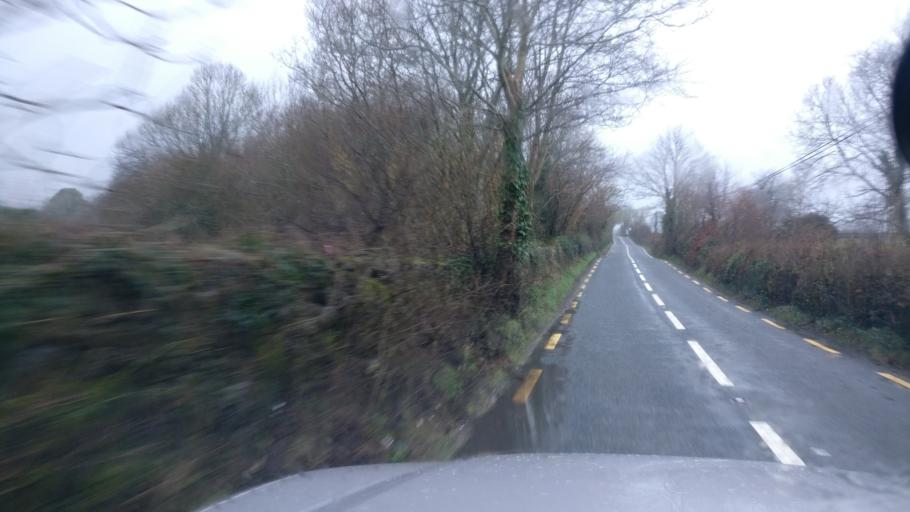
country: IE
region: Connaught
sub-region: County Galway
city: Loughrea
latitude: 53.1557
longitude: -8.4810
